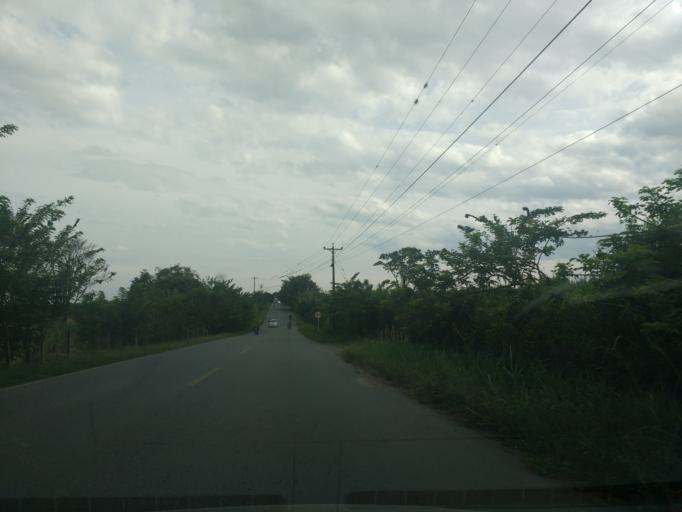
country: CO
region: Valle del Cauca
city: Florida
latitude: 3.2886
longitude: -76.2263
